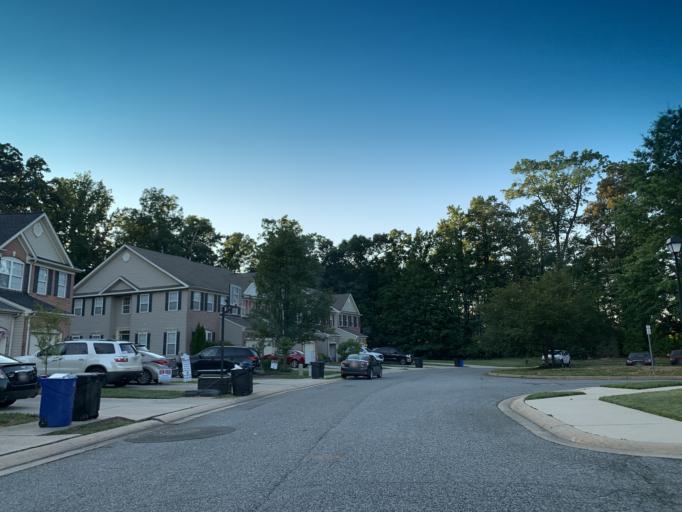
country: US
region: Maryland
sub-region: Harford County
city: Bel Air North
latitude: 39.5738
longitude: -76.3750
